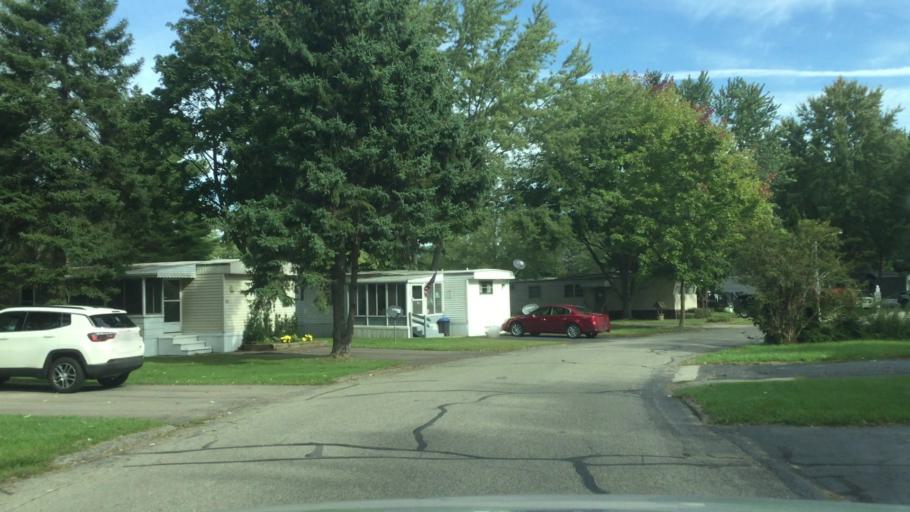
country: US
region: Michigan
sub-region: Oakland County
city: Holly
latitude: 42.8119
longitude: -83.6208
